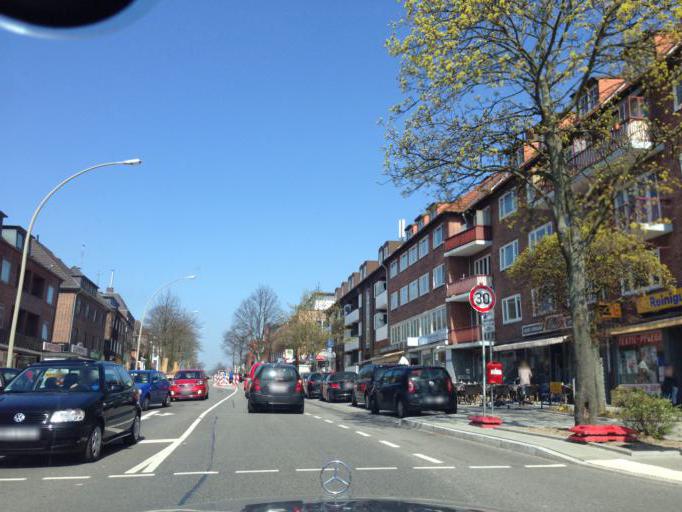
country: DE
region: Hamburg
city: Ohlsdorf
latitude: 53.6279
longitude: 10.0249
